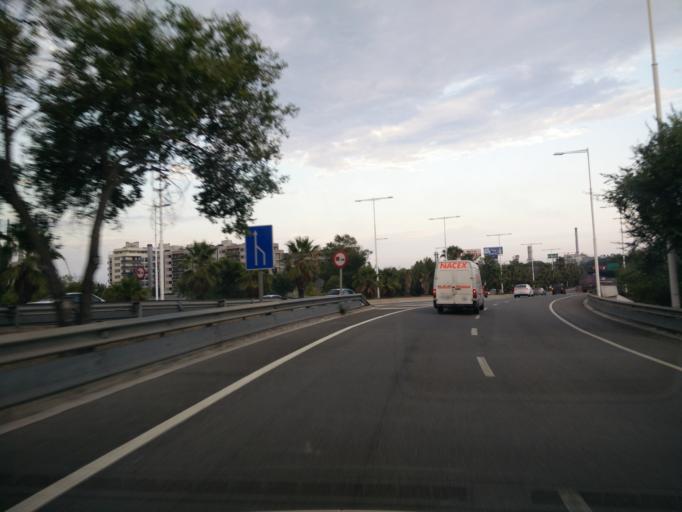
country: ES
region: Catalonia
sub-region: Provincia de Barcelona
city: Sant Adria de Besos
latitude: 41.4234
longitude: 2.2178
